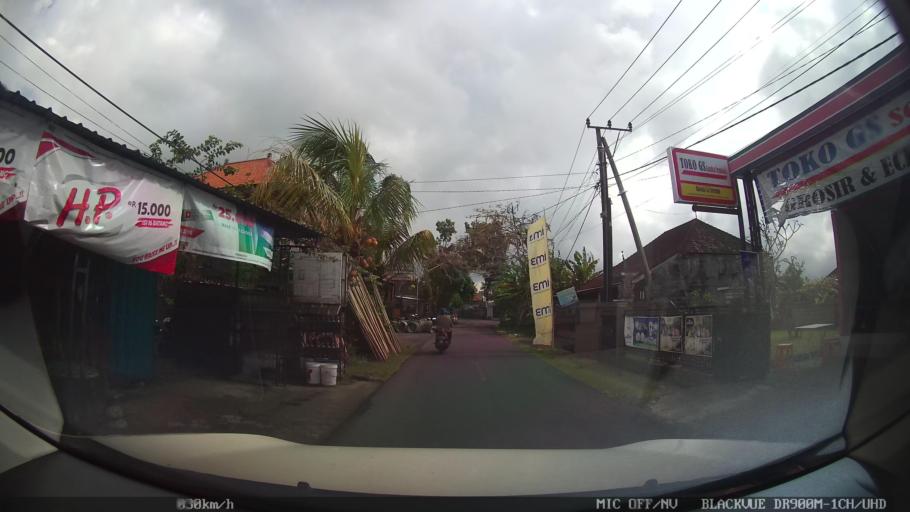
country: ID
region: Bali
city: Banjar Bucu
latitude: -8.5925
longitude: 115.2063
